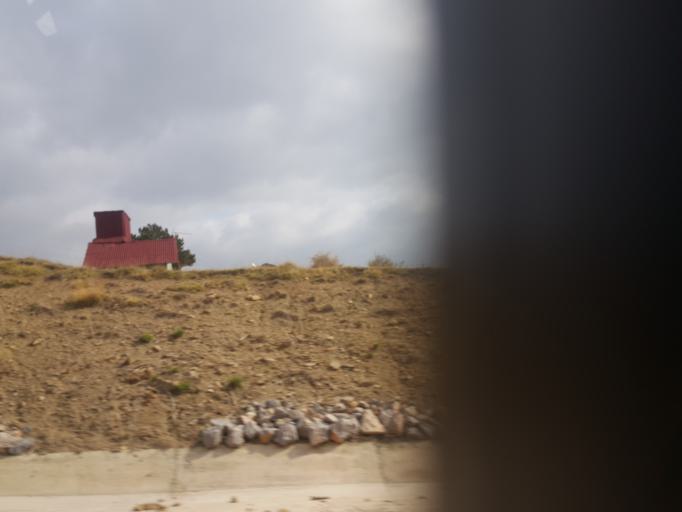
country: TR
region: Sinop
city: Duragan
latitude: 41.4993
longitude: 35.0347
